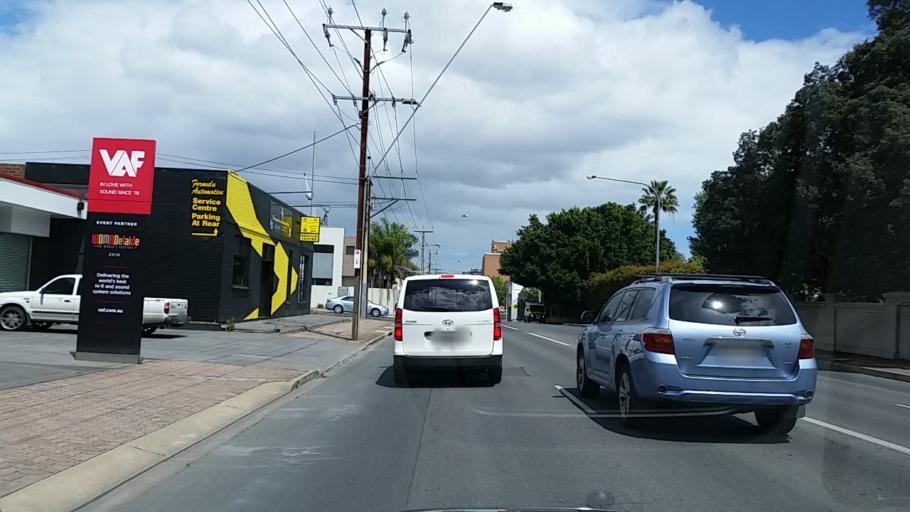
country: AU
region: South Australia
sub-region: Norwood Payneham St Peters
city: Trinity Gardens
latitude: -34.9173
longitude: 138.6195
